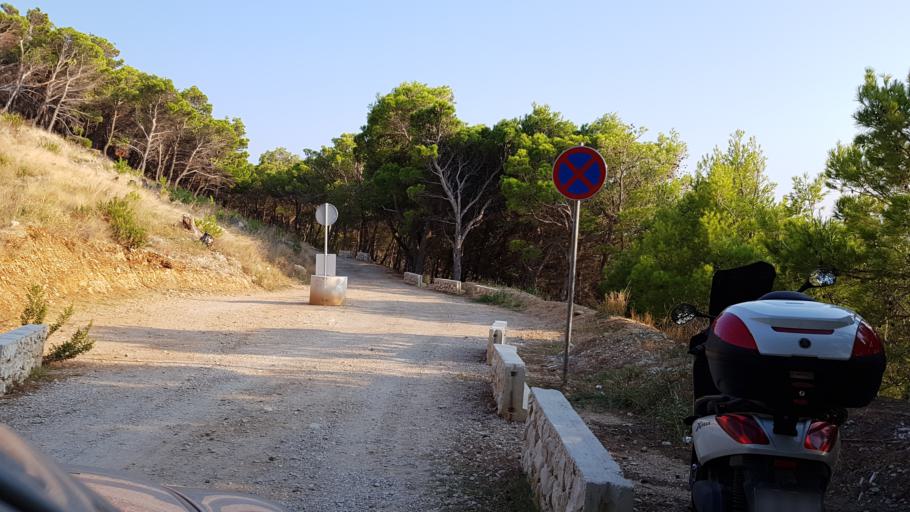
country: HR
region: Splitsko-Dalmatinska
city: Donja Brela
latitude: 43.3899
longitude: 16.8962
